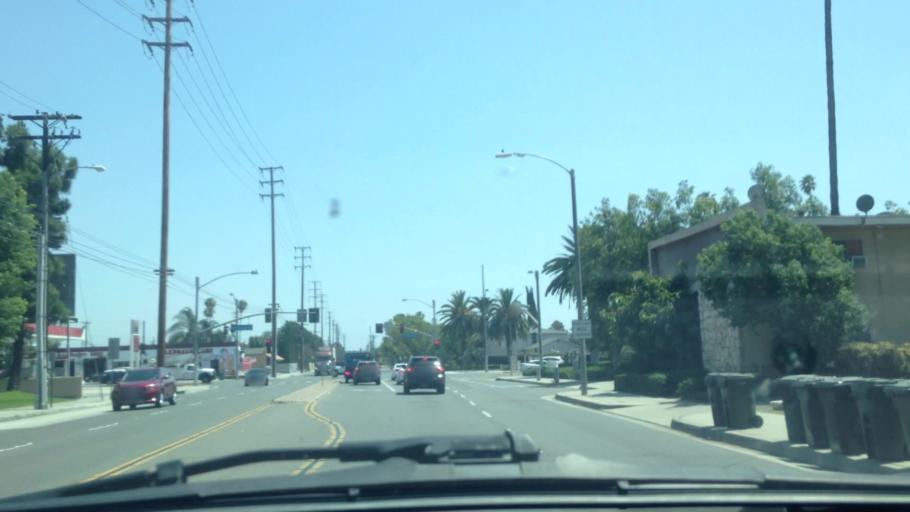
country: US
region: California
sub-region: Orange County
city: Anaheim
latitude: 33.8391
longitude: -117.9030
